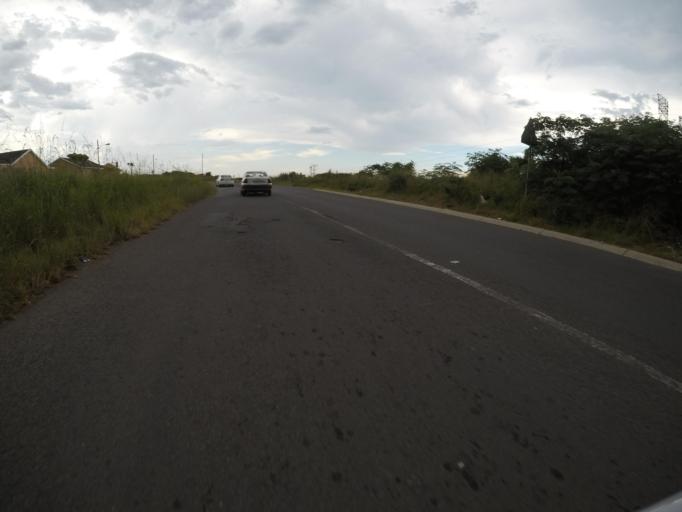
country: ZA
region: Eastern Cape
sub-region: Buffalo City Metropolitan Municipality
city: East London
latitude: -33.0250
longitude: 27.8644
